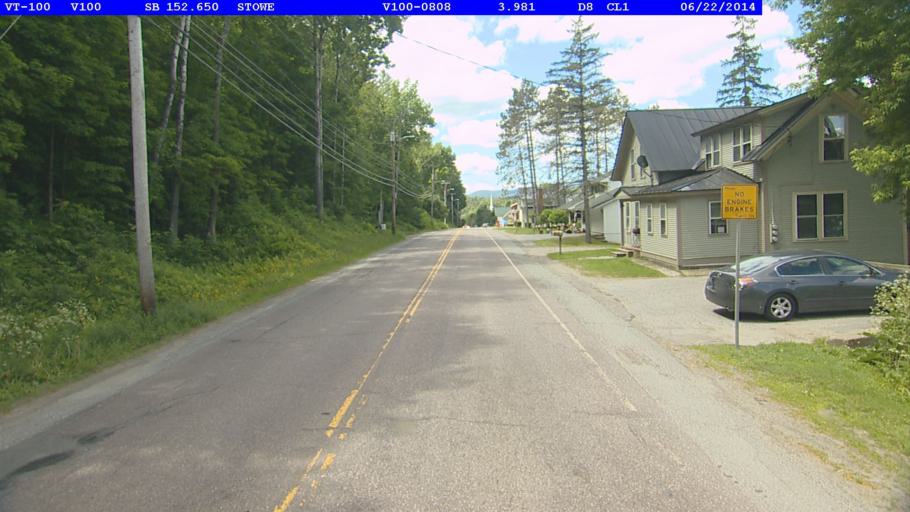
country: US
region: Vermont
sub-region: Lamoille County
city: Morristown
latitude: 44.4697
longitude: -72.6763
